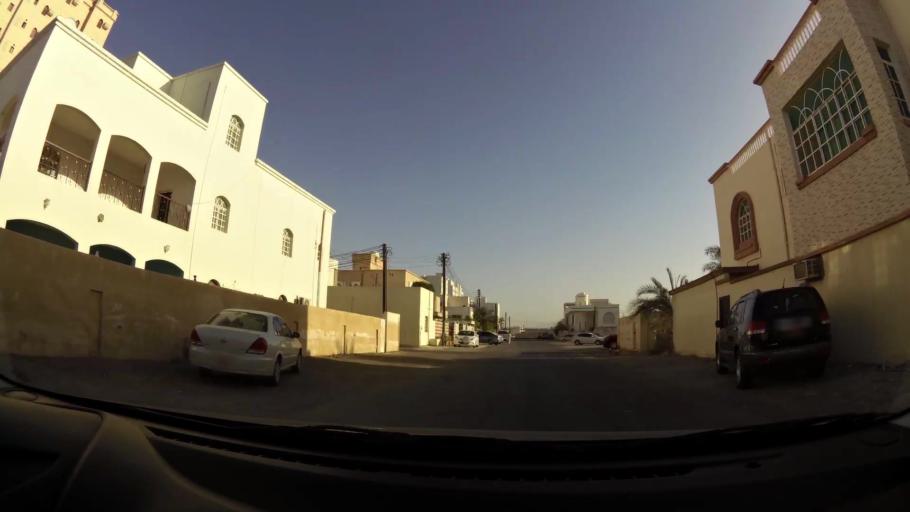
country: OM
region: Muhafazat Masqat
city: As Sib al Jadidah
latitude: 23.6292
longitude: 58.1957
